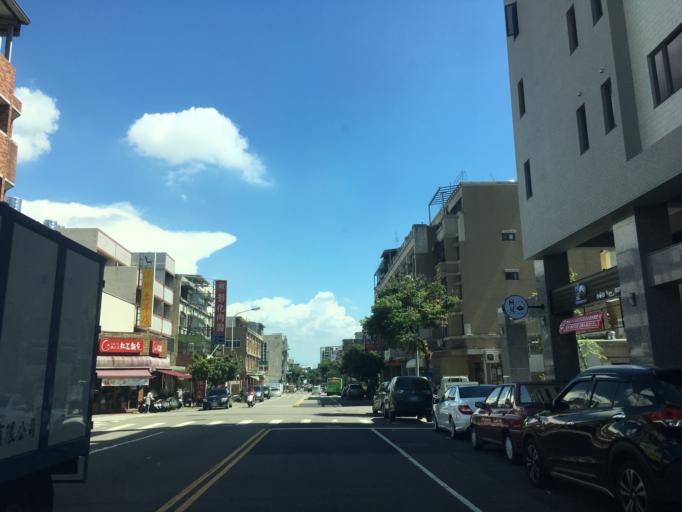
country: TW
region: Taiwan
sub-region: Taichung City
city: Taichung
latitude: 24.1441
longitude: 120.7061
